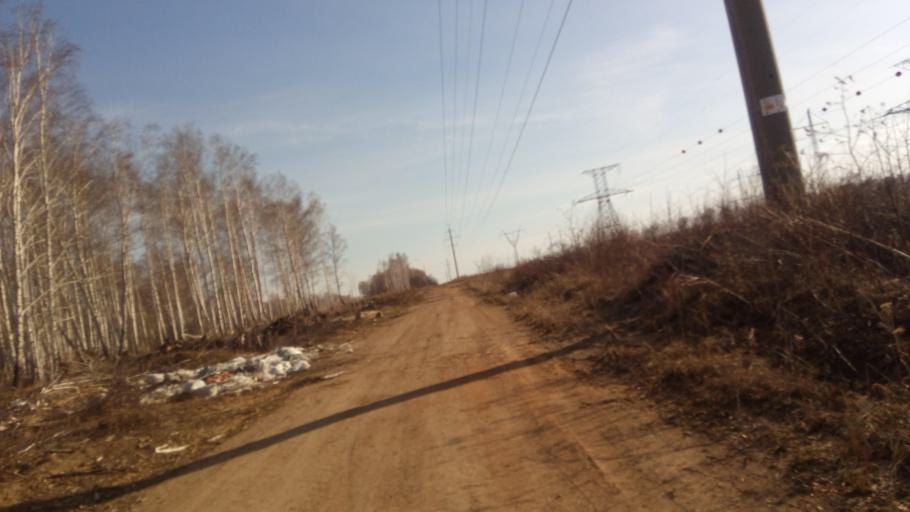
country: RU
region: Chelyabinsk
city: Sargazy
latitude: 55.1165
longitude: 61.2361
